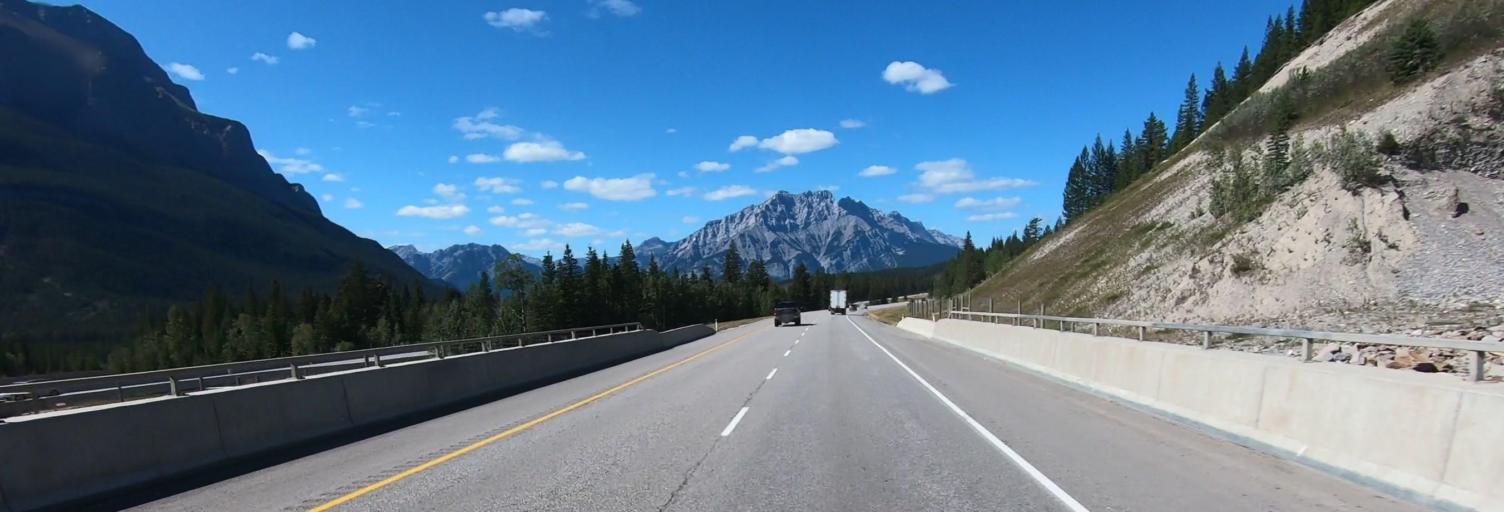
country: CA
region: Alberta
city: Canmore
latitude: 51.1489
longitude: -115.4304
